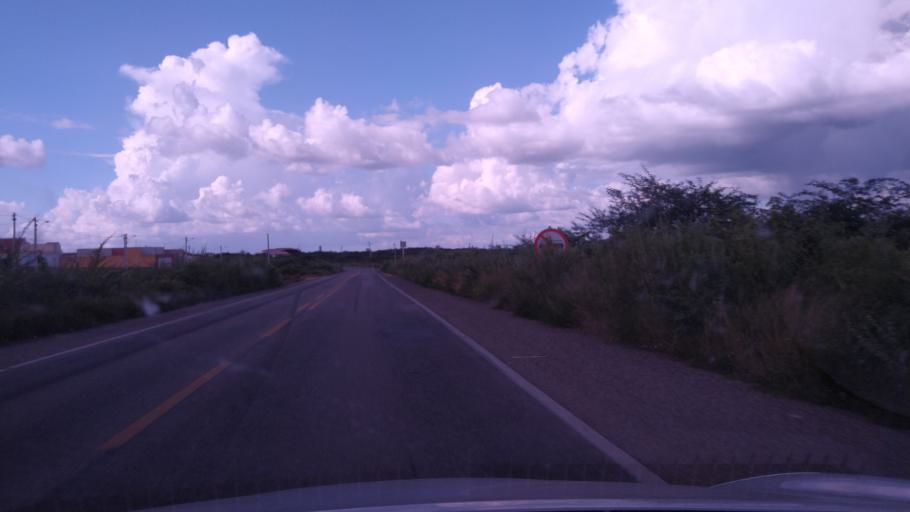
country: BR
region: Ceara
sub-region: Caninde
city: Caninde
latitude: -4.3970
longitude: -39.3164
